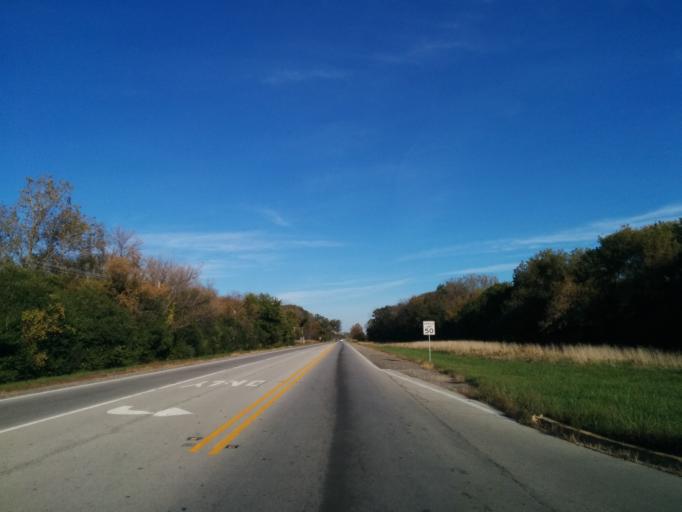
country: US
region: Illinois
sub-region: Kane County
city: Batavia
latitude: 41.8175
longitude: -88.2486
